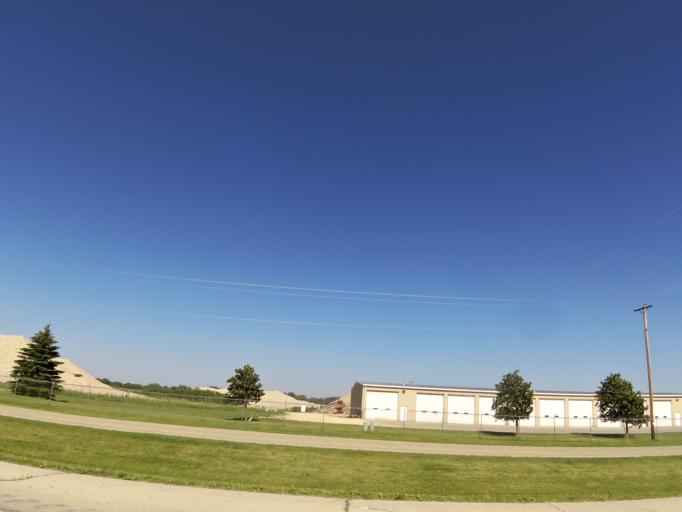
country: US
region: Illinois
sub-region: Winnebago County
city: South Beloit
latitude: 42.4751
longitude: -89.0194
